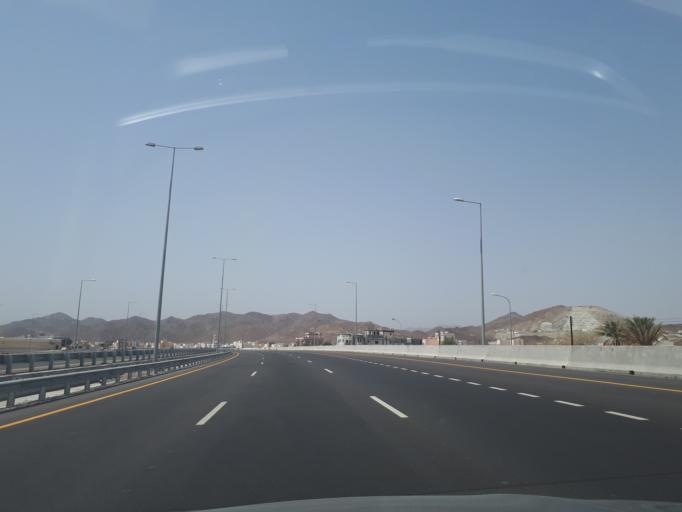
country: OM
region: Muhafazat ad Dakhiliyah
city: Bidbid
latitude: 23.4067
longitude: 58.0990
